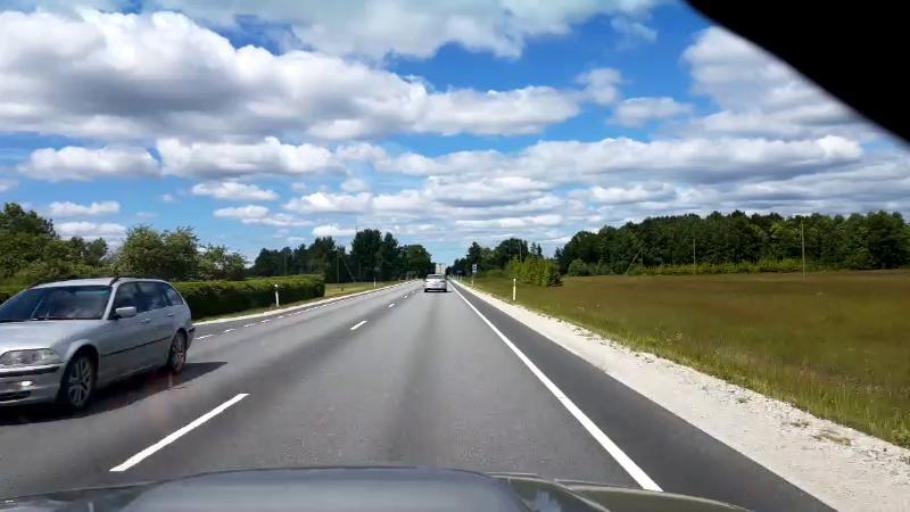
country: EE
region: Paernumaa
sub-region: Halinga vald
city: Parnu-Jaagupi
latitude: 58.6521
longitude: 24.4785
